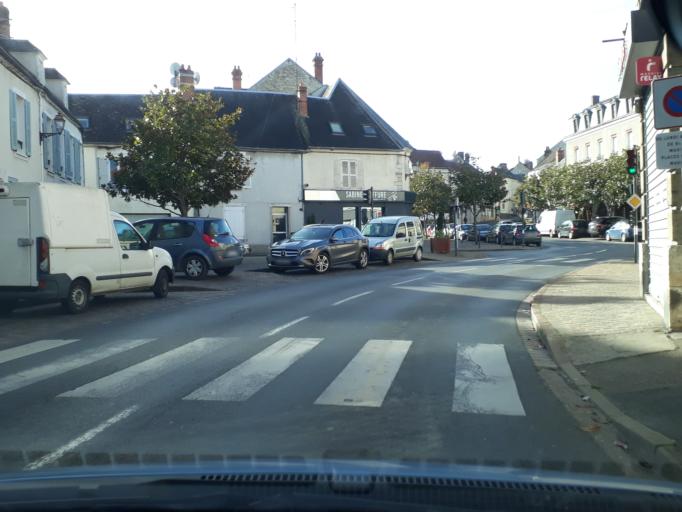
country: FR
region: Centre
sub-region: Departement du Loiret
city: Malesherbes
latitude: 48.2973
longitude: 2.4156
